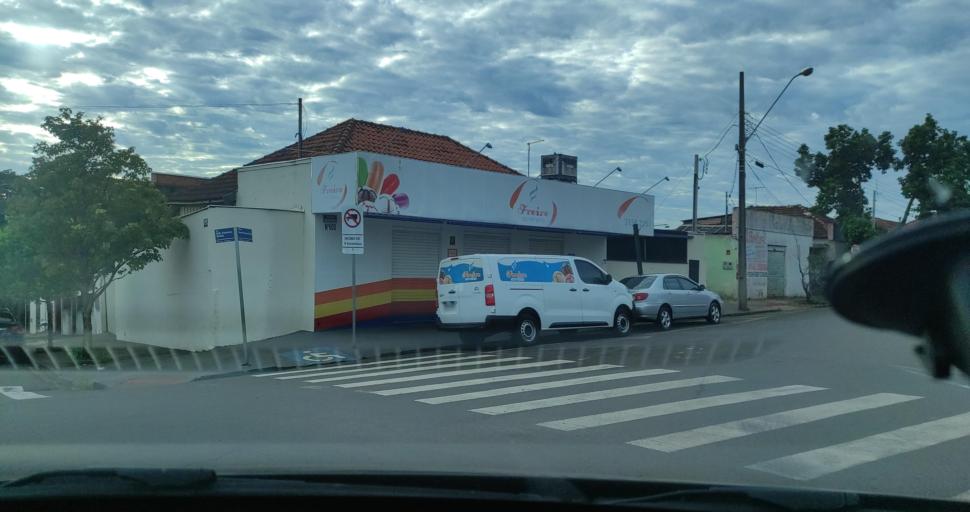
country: BR
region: Parana
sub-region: Ibipora
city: Ibipora
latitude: -23.2675
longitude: -51.0444
